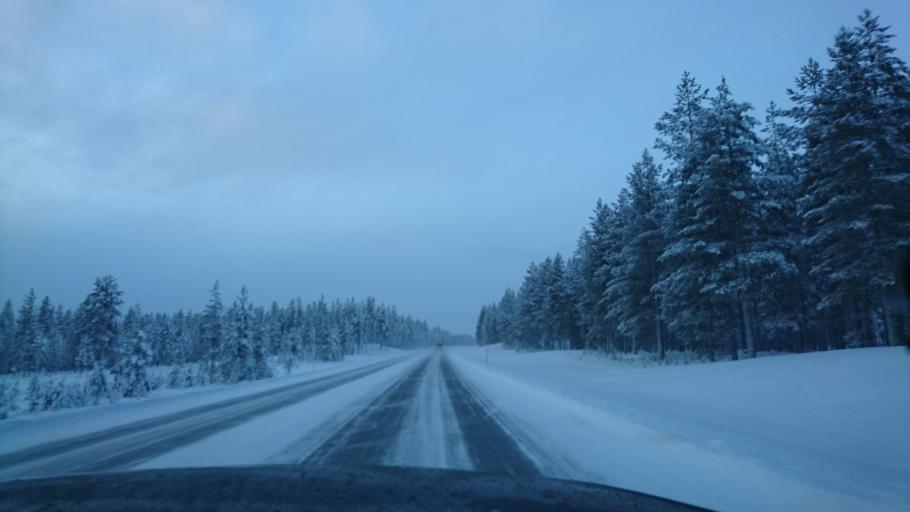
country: FI
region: Kainuu
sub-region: Kehys-Kainuu
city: Puolanka
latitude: 65.4348
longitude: 27.5868
